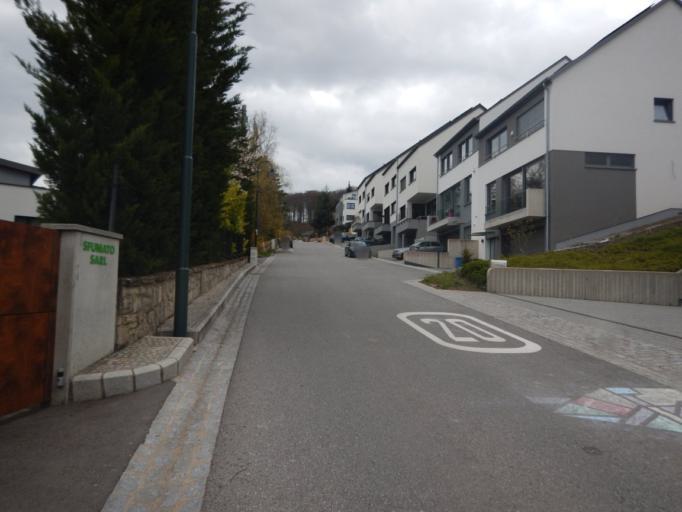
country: LU
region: Luxembourg
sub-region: Canton de Mersch
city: Lorentzweiler
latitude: 49.7039
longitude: 6.1431
